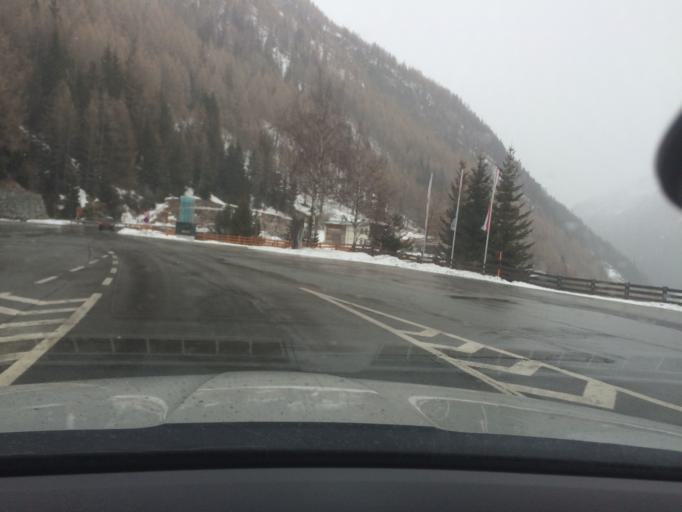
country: AT
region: Tyrol
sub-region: Politischer Bezirk Lienz
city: Matrei in Osttirol
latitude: 47.1175
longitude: 12.5046
